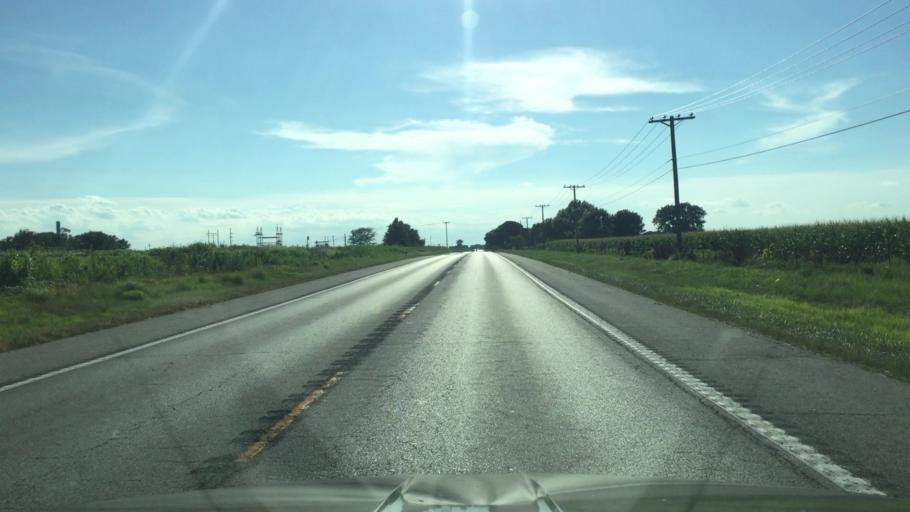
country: US
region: Missouri
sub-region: Pettis County
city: Sedalia
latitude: 38.6948
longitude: -93.1455
